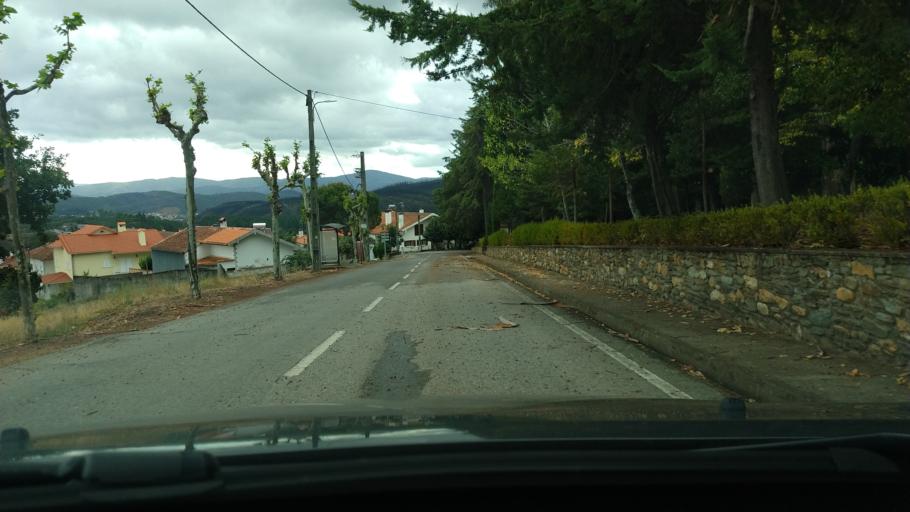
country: PT
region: Castelo Branco
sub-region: Covilha
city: Covilha
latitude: 40.2284
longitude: -7.6474
